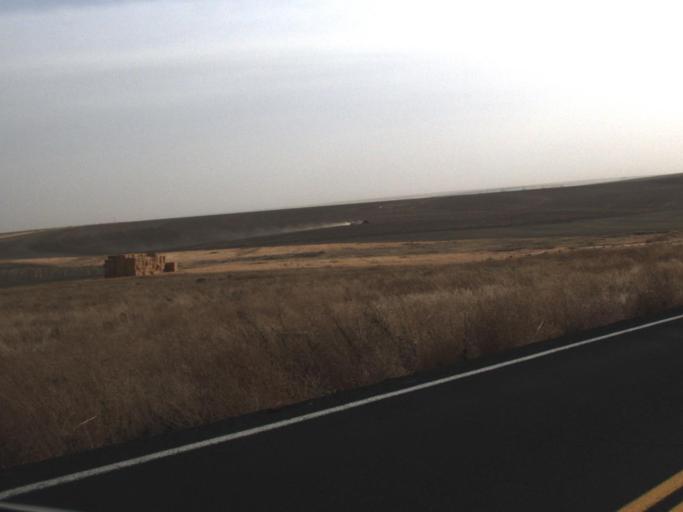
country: US
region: Washington
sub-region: Adams County
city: Ritzville
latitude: 47.3839
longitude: -118.6904
